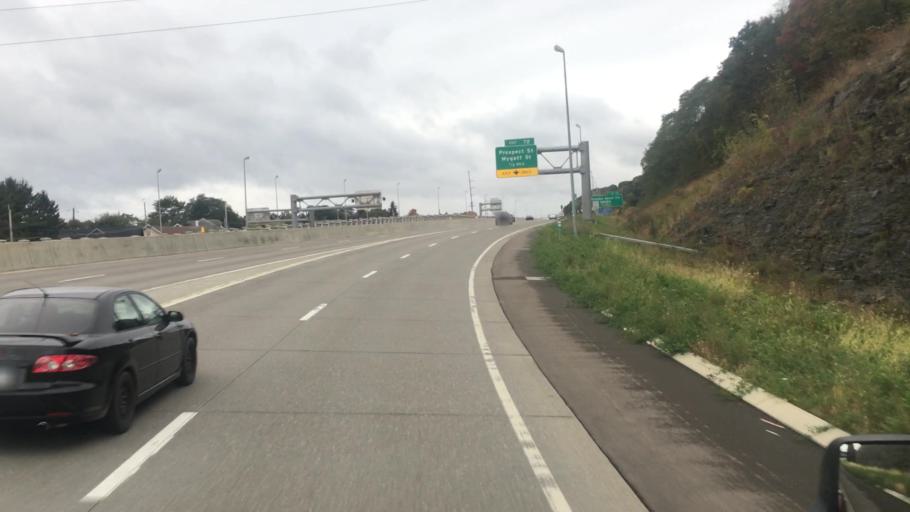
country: US
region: New York
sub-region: Broome County
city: Binghamton
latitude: 42.1118
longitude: -75.9145
